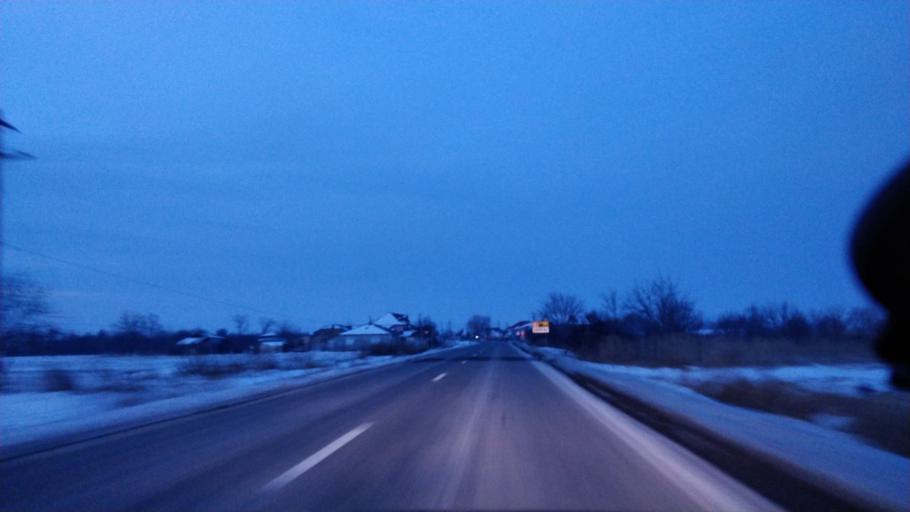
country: RO
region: Vrancea
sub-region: Comuna Nanesti
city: Nanesti
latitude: 45.5841
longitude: 27.4967
